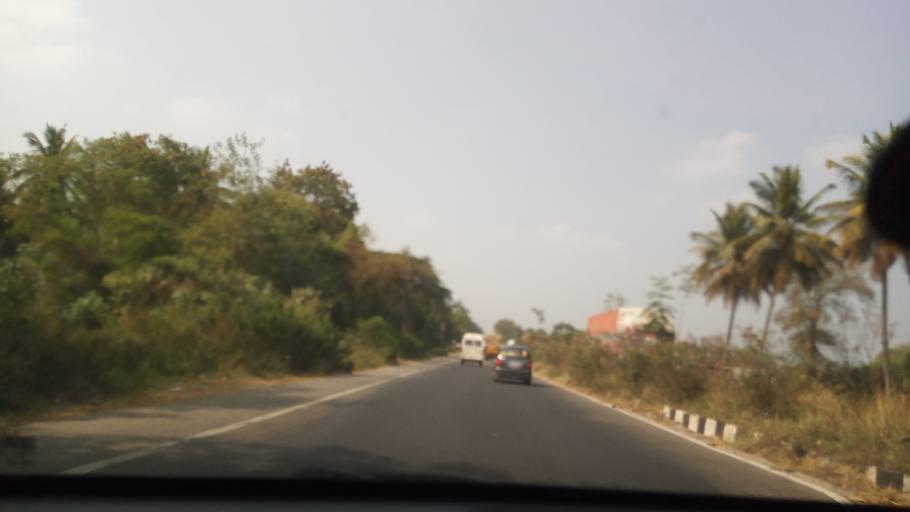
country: IN
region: Karnataka
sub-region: Mysore
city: Nanjangud
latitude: 12.1826
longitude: 76.6689
